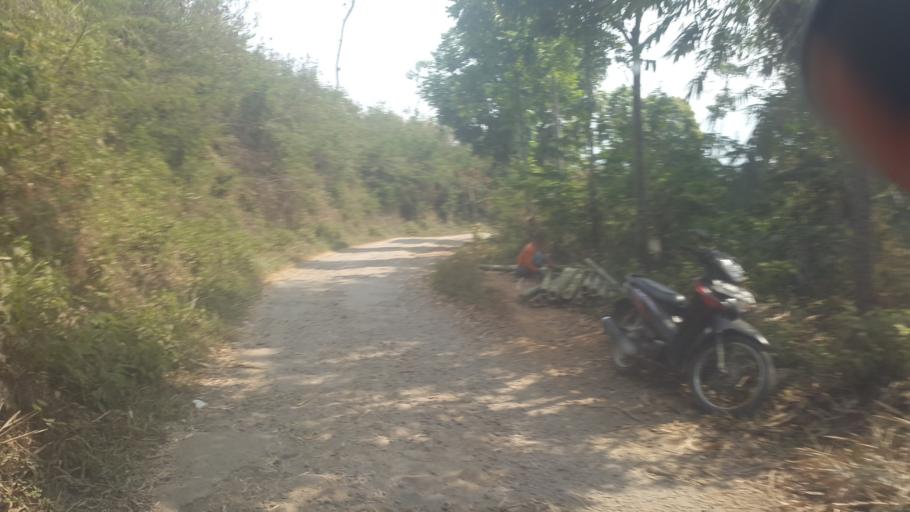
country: ID
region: West Java
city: Cijapar
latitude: -6.8775
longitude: 106.4425
